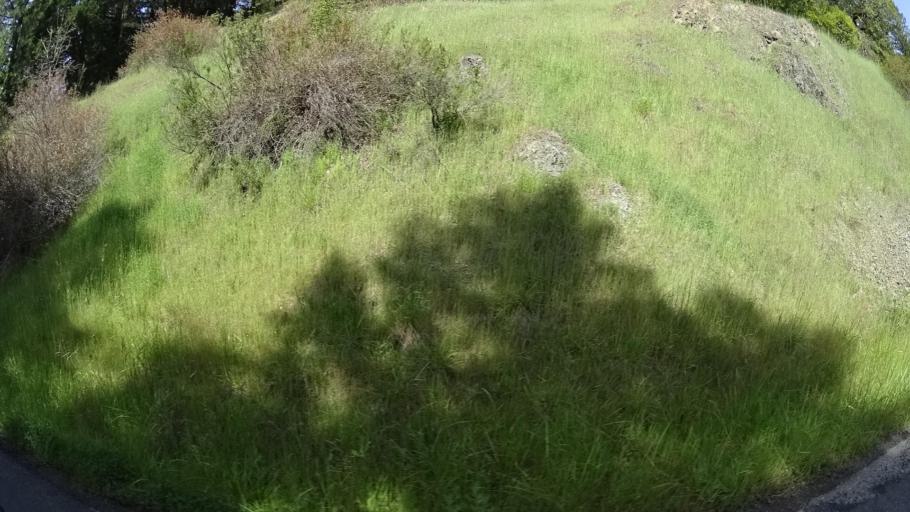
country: US
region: California
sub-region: Humboldt County
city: Redway
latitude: 40.4326
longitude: -123.7661
